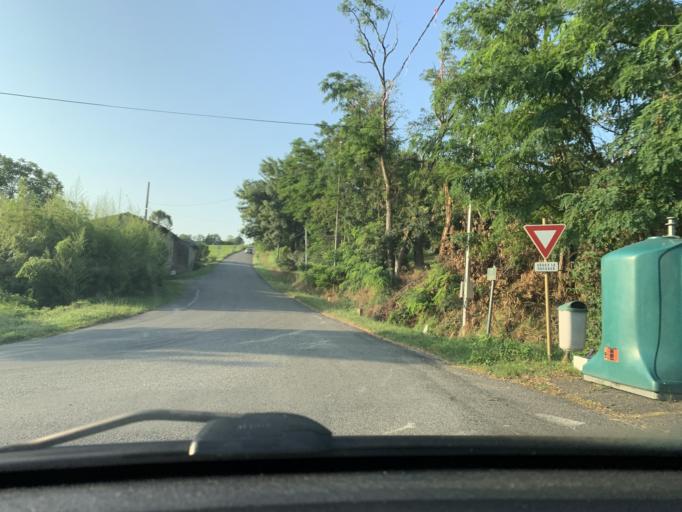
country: FR
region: Midi-Pyrenees
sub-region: Departement de la Haute-Garonne
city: Auzielle
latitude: 43.5273
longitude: 1.5886
